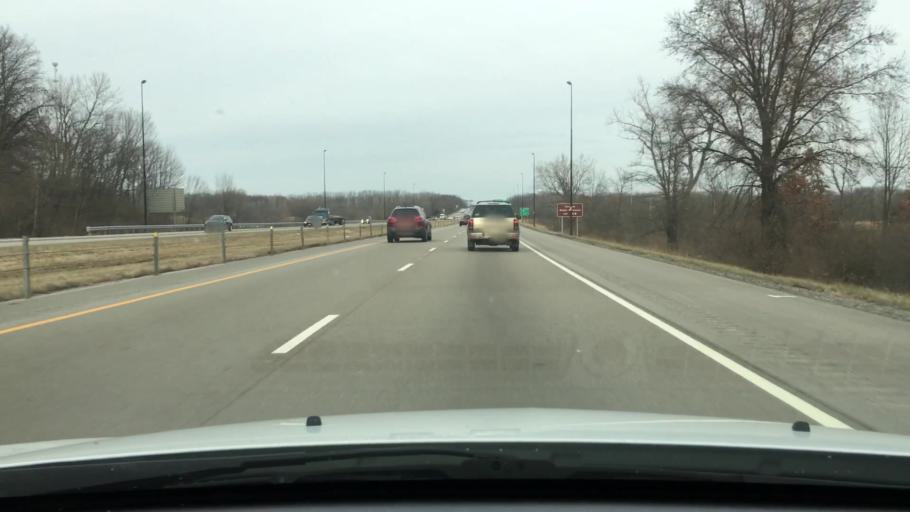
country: US
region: Illinois
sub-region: Sangamon County
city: Grandview
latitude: 39.7737
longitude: -89.6026
